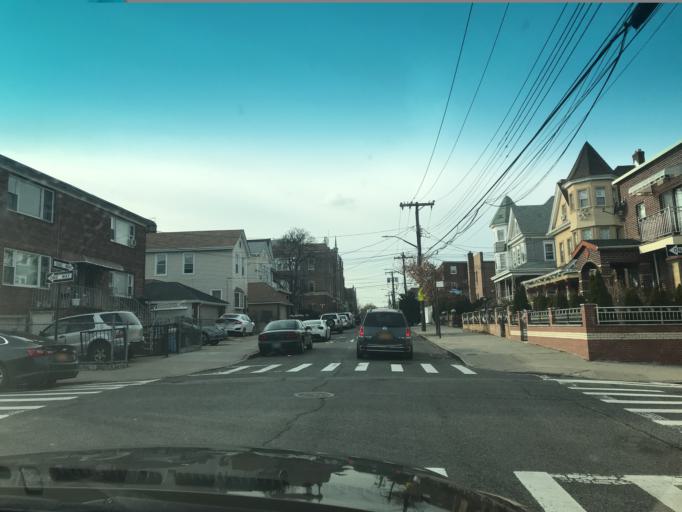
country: US
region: New York
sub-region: Bronx
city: The Bronx
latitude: 40.7853
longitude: -73.8418
